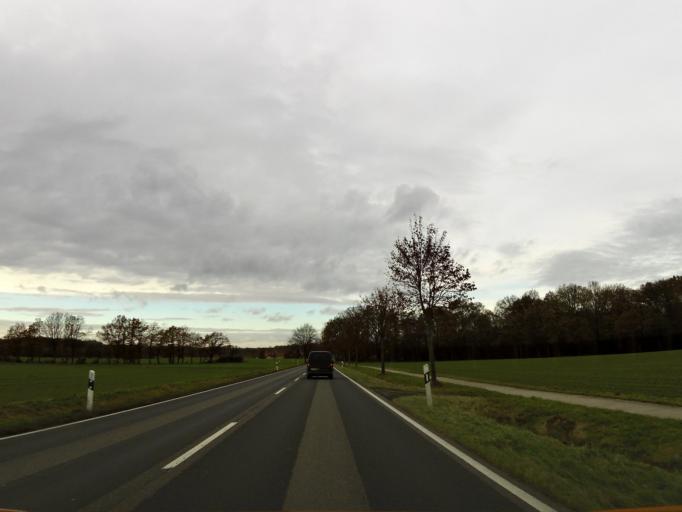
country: DE
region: Lower Saxony
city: Gerdau
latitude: 52.9600
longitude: 10.4229
